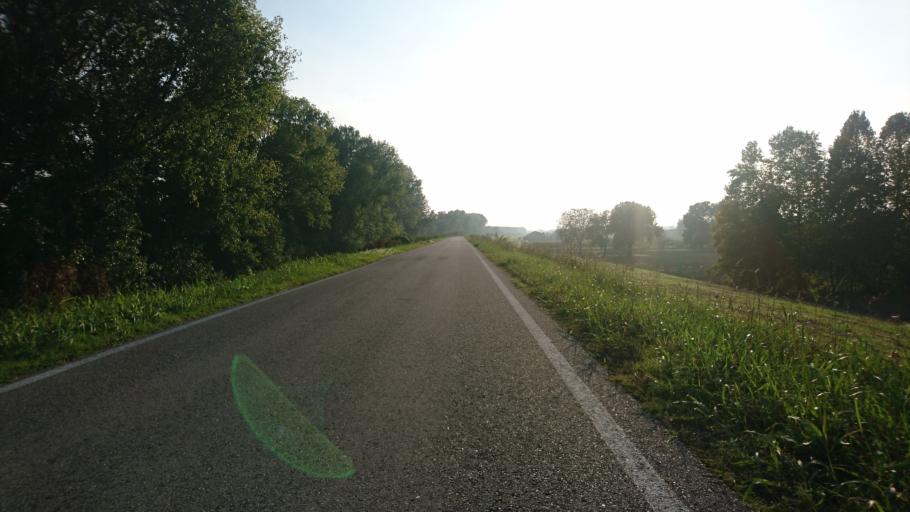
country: IT
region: Emilia-Romagna
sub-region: Provincia di Ferrara
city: Francolino
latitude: 44.9034
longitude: 11.6462
